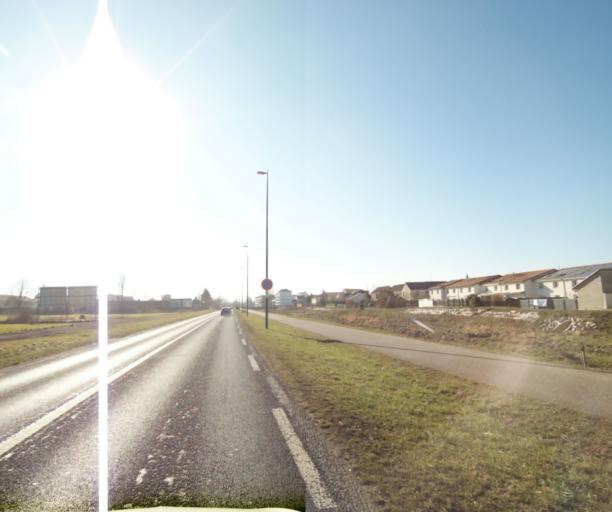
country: FR
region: Lorraine
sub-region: Departement de Meurthe-et-Moselle
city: Essey-les-Nancy
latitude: 48.7059
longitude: 6.2359
